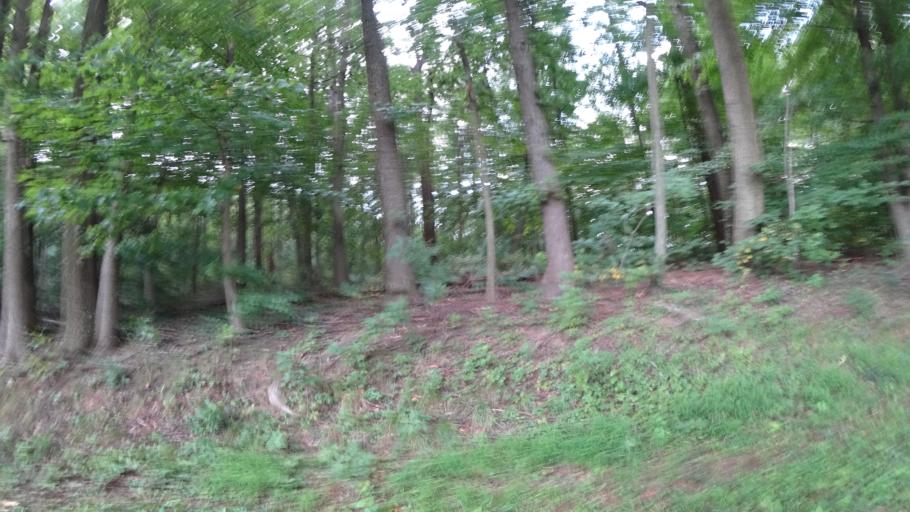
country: US
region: Maryland
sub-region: Prince George's County
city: Mount Rainier
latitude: 38.9123
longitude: -76.9745
